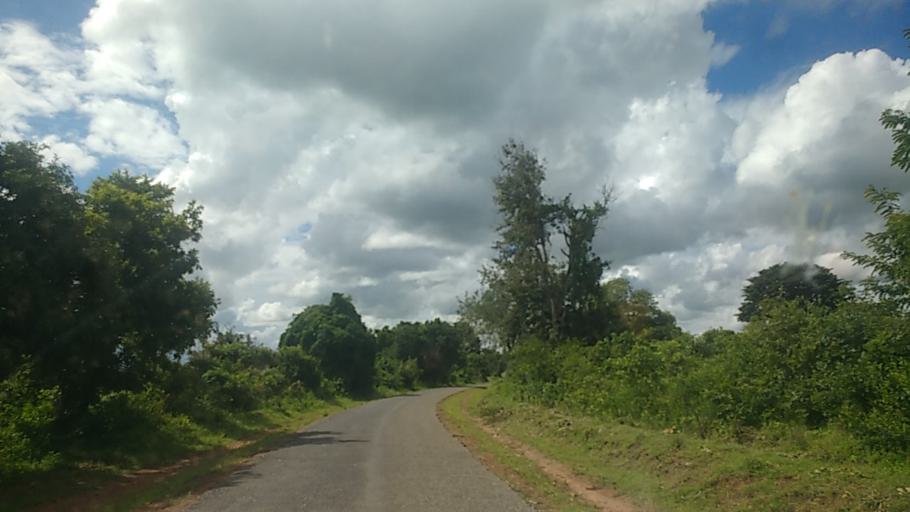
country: UG
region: Eastern Region
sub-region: Katakwi District
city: Katakwi
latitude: 1.8997
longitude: 33.9601
